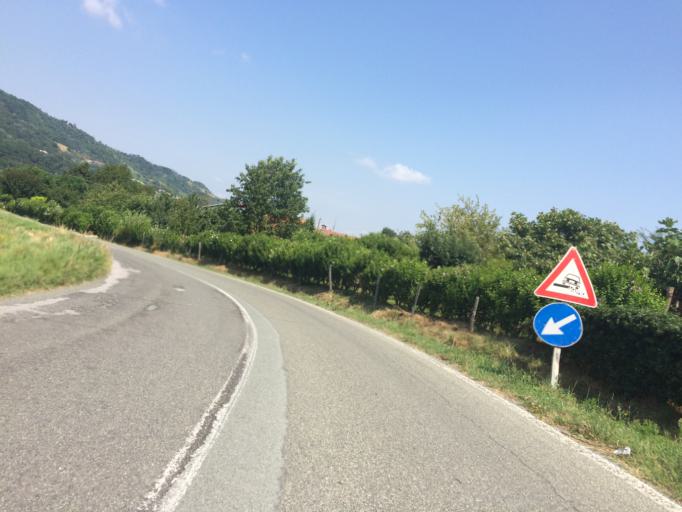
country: IT
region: Piedmont
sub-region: Provincia di Alessandria
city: Melazzo
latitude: 44.6243
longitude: 8.4164
